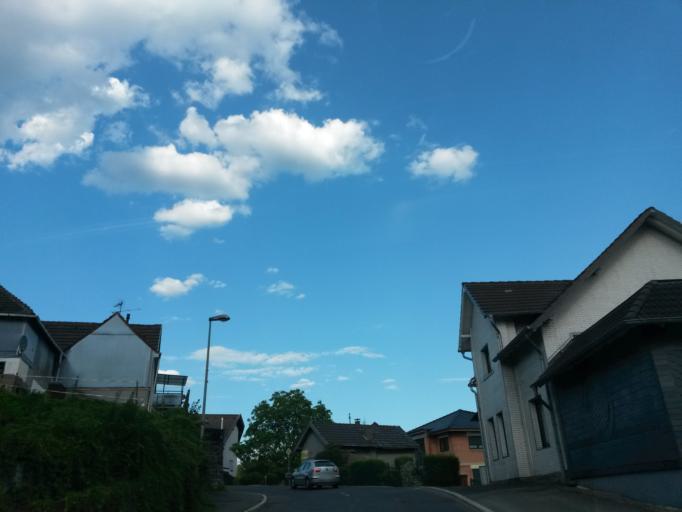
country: DE
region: North Rhine-Westphalia
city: Wiehl
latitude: 50.9694
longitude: 7.5118
